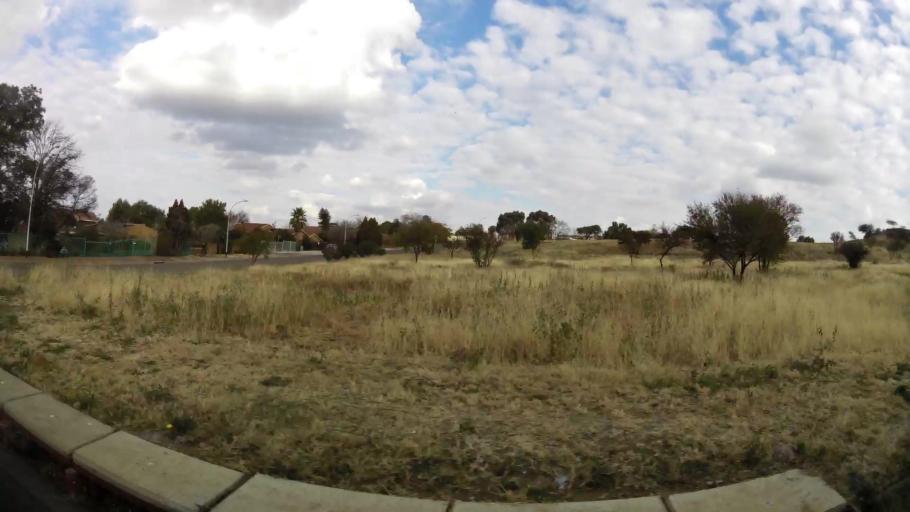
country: ZA
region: Orange Free State
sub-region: Mangaung Metropolitan Municipality
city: Bloemfontein
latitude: -29.0812
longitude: 26.2048
